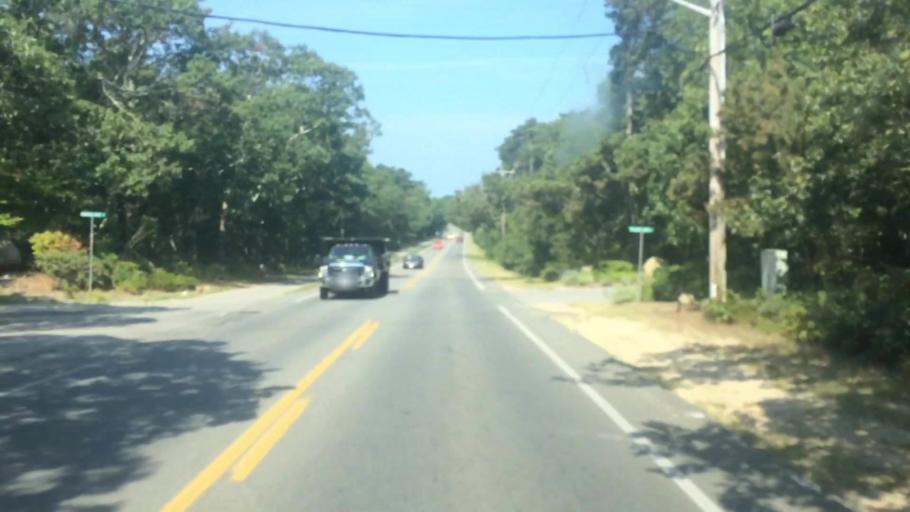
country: US
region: Massachusetts
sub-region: Dukes County
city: Oak Bluffs
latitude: 41.4118
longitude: -70.5747
